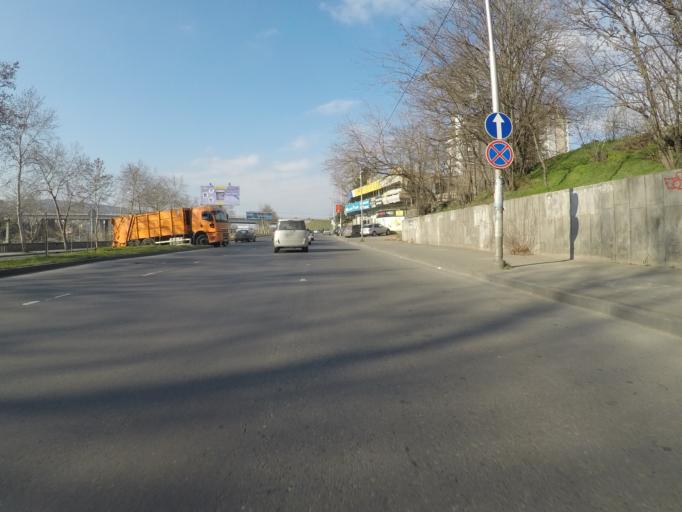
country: GE
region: T'bilisi
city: Tbilisi
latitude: 41.7233
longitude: 44.7839
